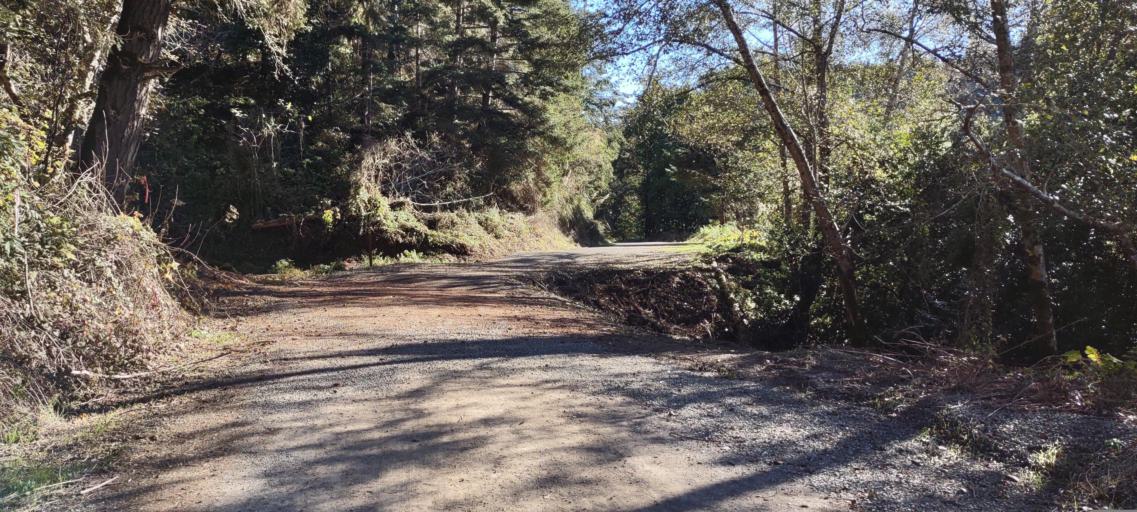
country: US
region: California
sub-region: Mendocino County
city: Fort Bragg
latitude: 39.3046
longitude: -123.7765
